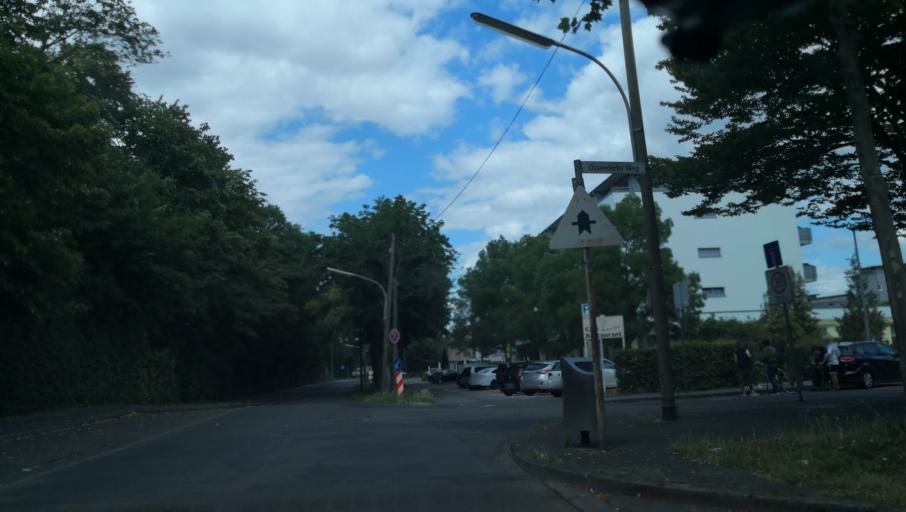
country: DE
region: North Rhine-Westphalia
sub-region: Regierungsbezirk Koln
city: Mengenich
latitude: 50.9693
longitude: 6.8844
